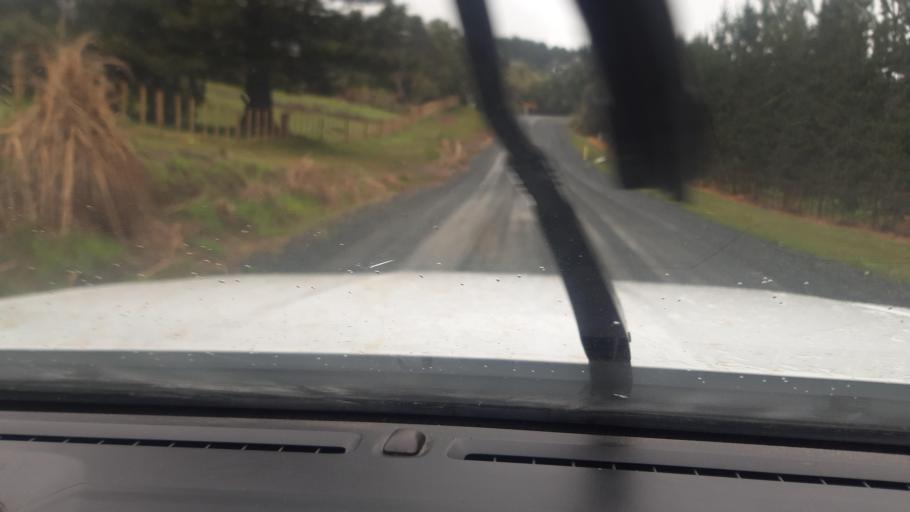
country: NZ
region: Northland
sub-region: Far North District
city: Kaitaia
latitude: -34.9767
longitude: 173.2033
